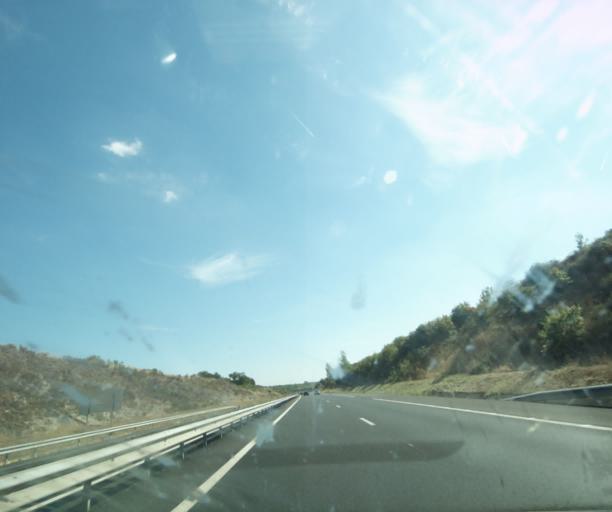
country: FR
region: Limousin
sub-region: Departement de la Correze
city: Brive-la-Gaillarde
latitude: 45.0511
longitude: 1.5123
